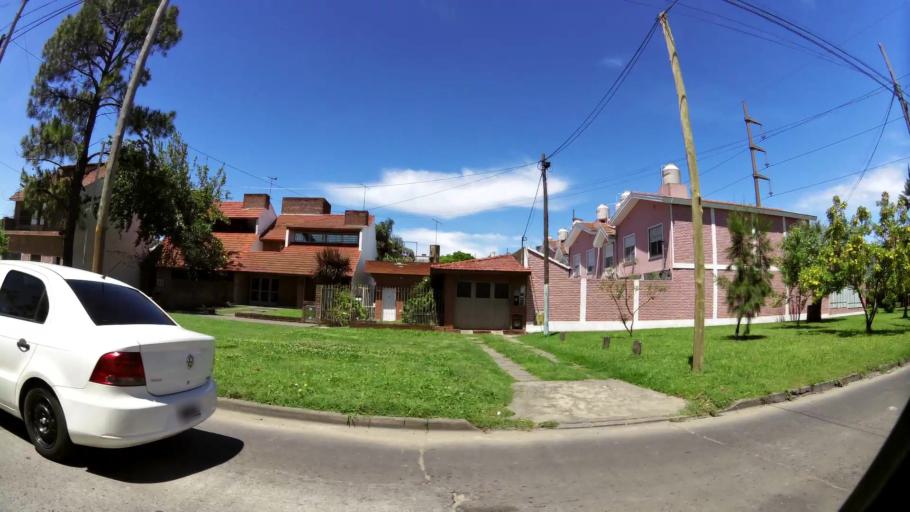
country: AR
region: Buenos Aires
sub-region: Partido de Quilmes
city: Quilmes
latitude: -34.7350
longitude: -58.2839
